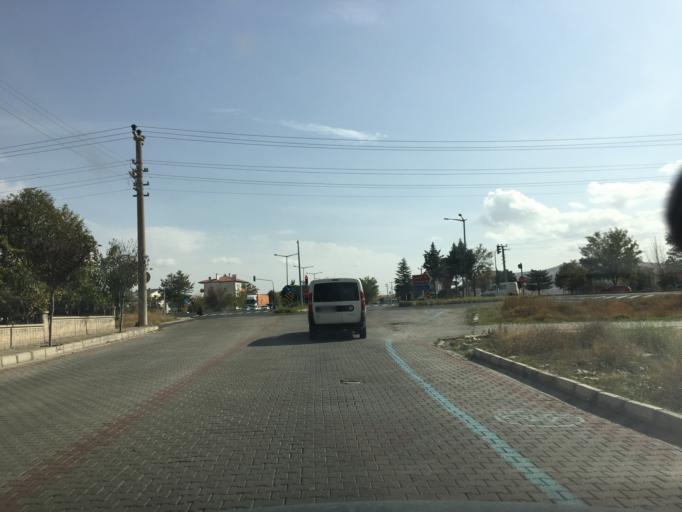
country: TR
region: Nevsehir
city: Avanos
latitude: 38.7055
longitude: 34.8544
